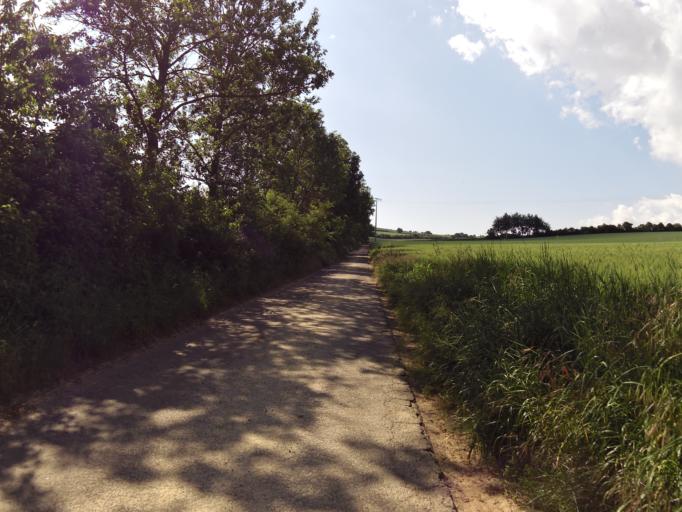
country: DE
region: Rheinland-Pfalz
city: Tiefenthal
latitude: 49.5507
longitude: 8.1103
